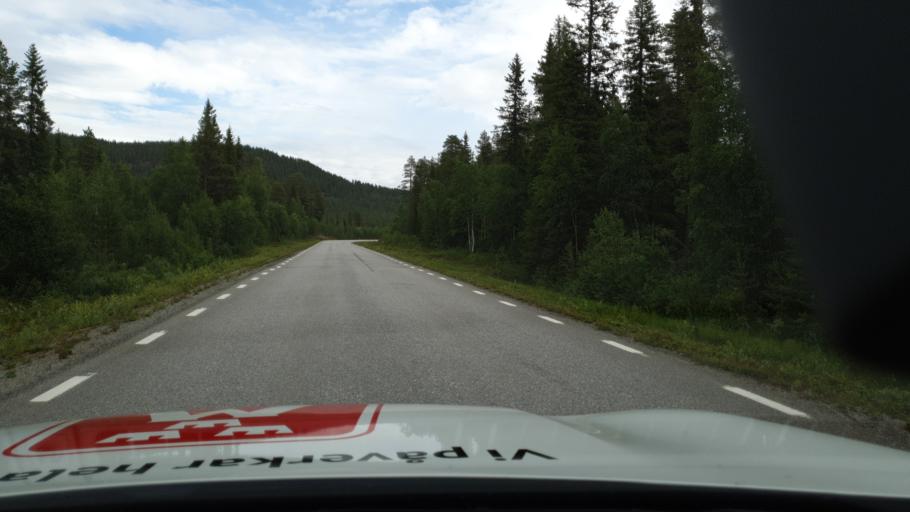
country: SE
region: Vaesterbotten
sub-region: Sorsele Kommun
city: Sorsele
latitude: 65.5443
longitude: 17.4128
